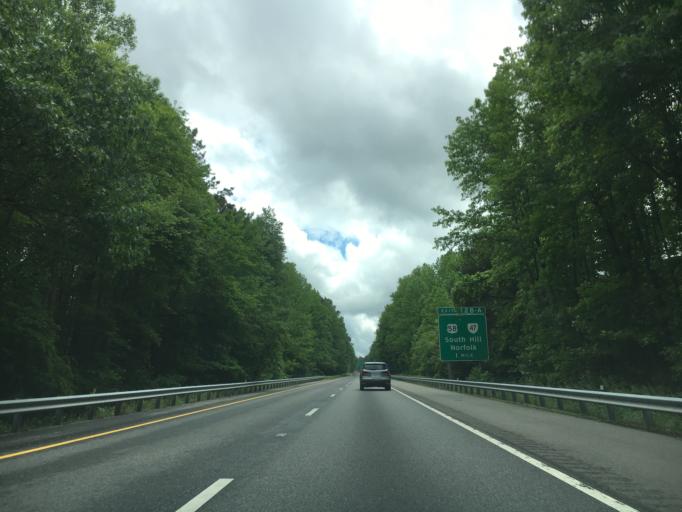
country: US
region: Virginia
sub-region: Mecklenburg County
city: South Hill
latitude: 36.7304
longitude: -78.1052
